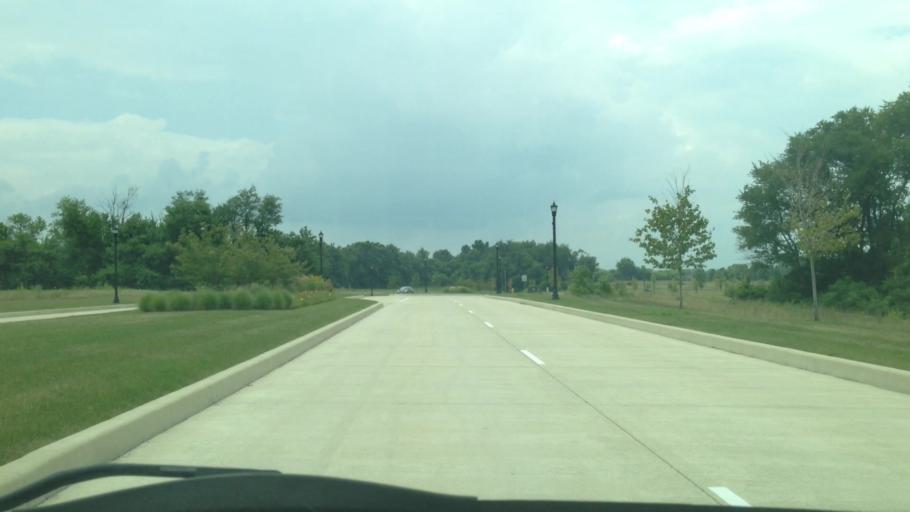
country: US
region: Indiana
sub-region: Saint Joseph County
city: Granger
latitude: 41.7294
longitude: -86.1515
